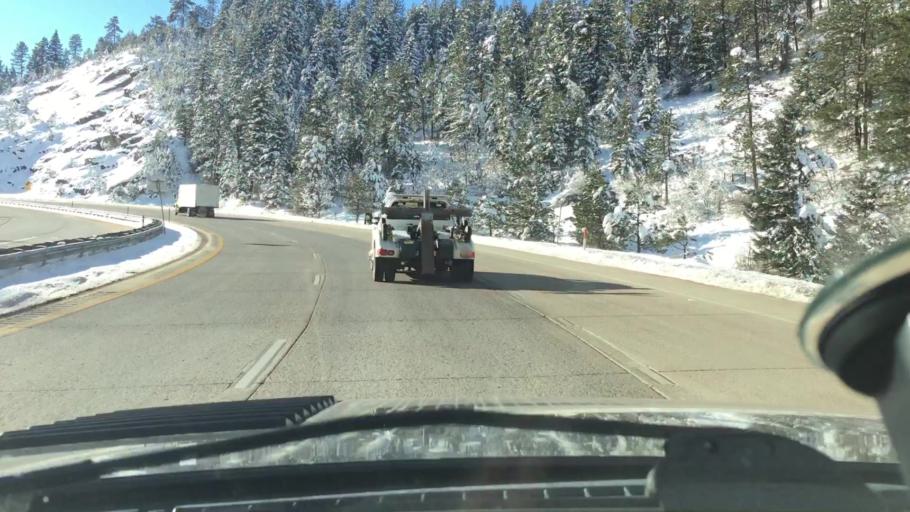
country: US
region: Colorado
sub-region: Jefferson County
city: Indian Hills
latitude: 39.6152
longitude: -105.2330
